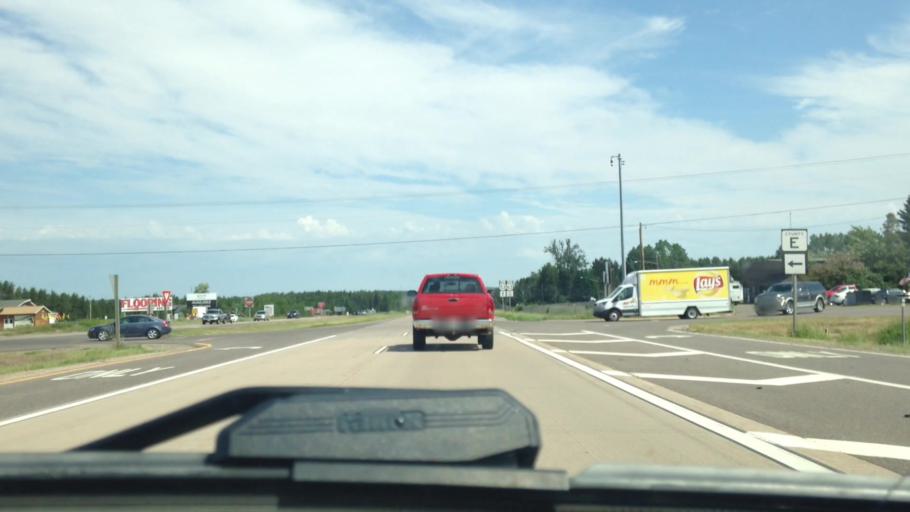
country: US
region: Wisconsin
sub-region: Washburn County
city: Spooner
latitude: 45.8991
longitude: -91.8277
